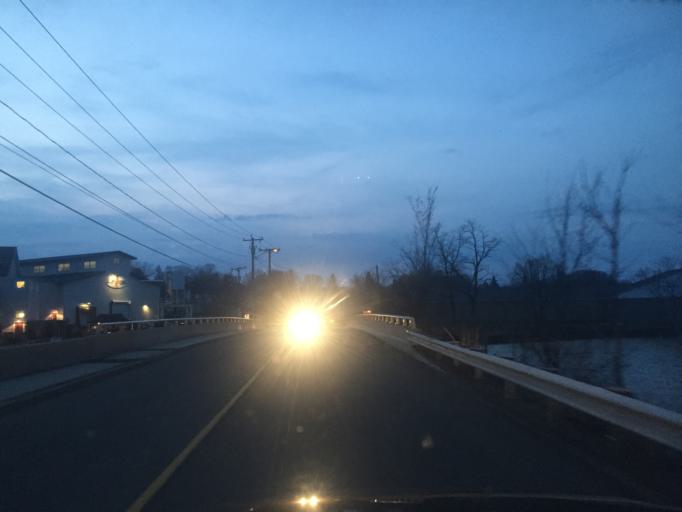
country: US
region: Connecticut
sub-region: New Haven County
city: Branford Center
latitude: 41.2742
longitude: -72.8117
